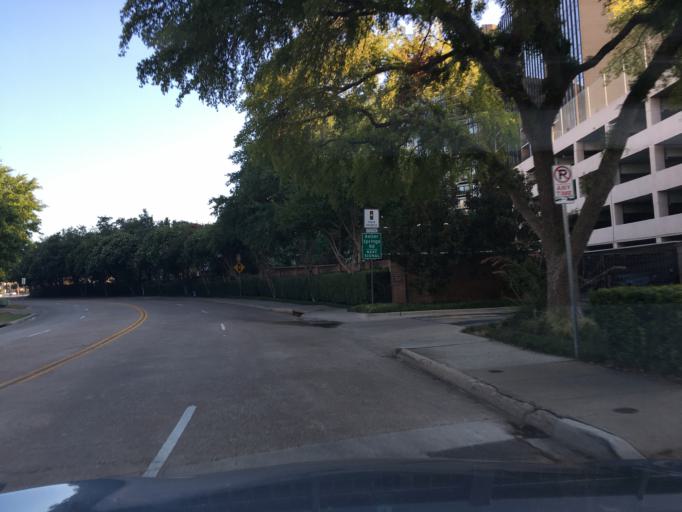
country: US
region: Texas
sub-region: Dallas County
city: Addison
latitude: 32.9667
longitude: -96.8189
